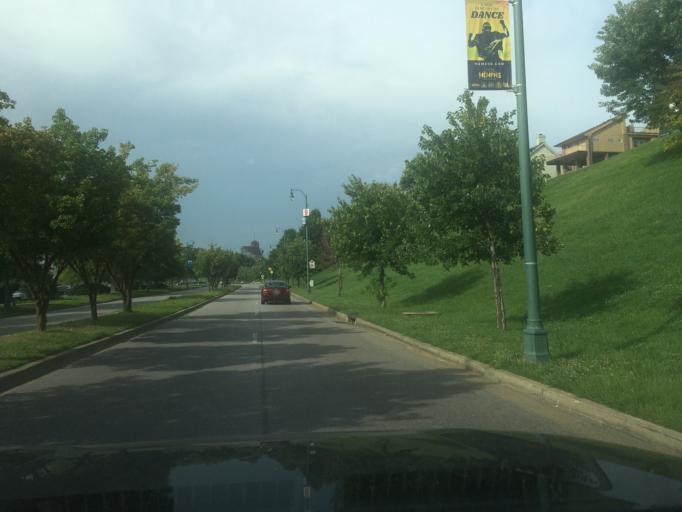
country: US
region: Tennessee
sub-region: Shelby County
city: Memphis
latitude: 35.1353
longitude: -90.0634
